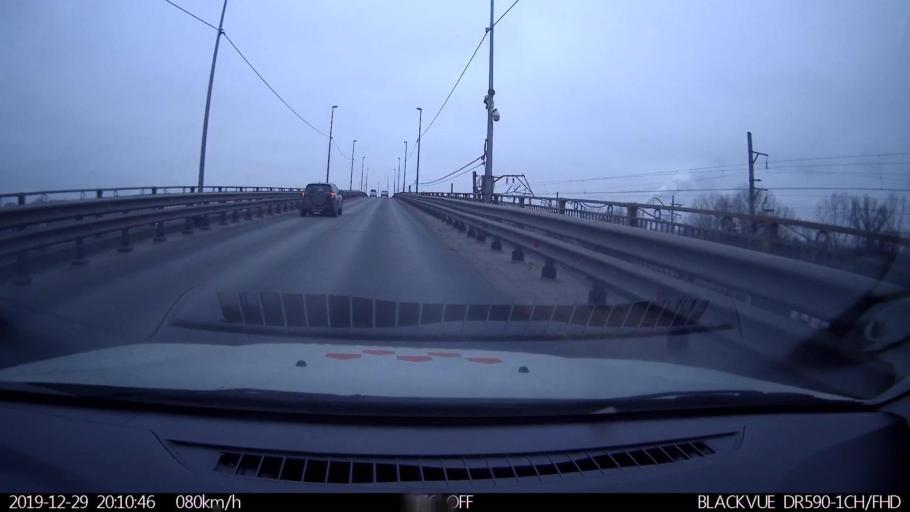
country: RU
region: Nizjnij Novgorod
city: Neklyudovo
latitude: 56.3622
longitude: 43.9319
